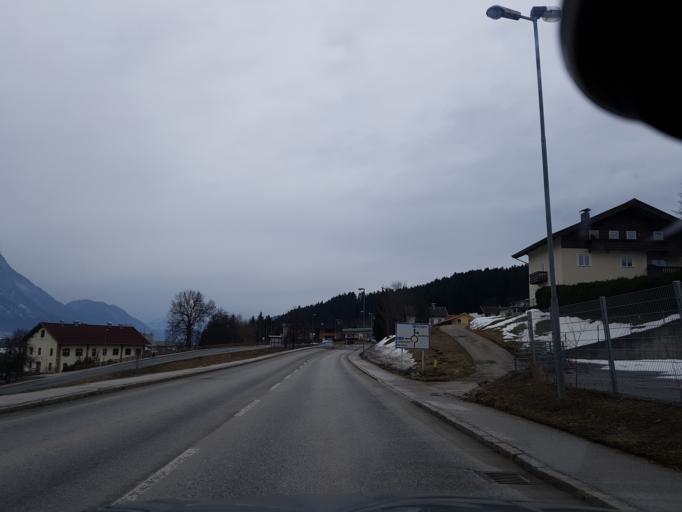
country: AT
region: Tyrol
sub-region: Politischer Bezirk Kufstein
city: Bad Haering
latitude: 47.5173
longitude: 12.0958
